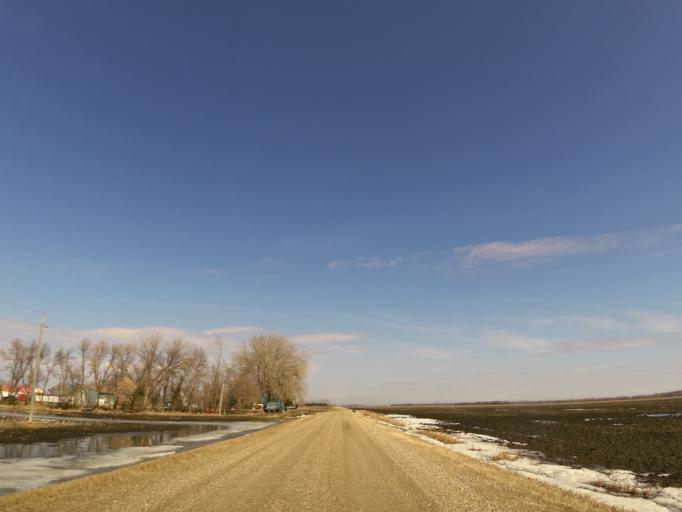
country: US
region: North Dakota
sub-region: Walsh County
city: Grafton
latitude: 48.4057
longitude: -97.1685
